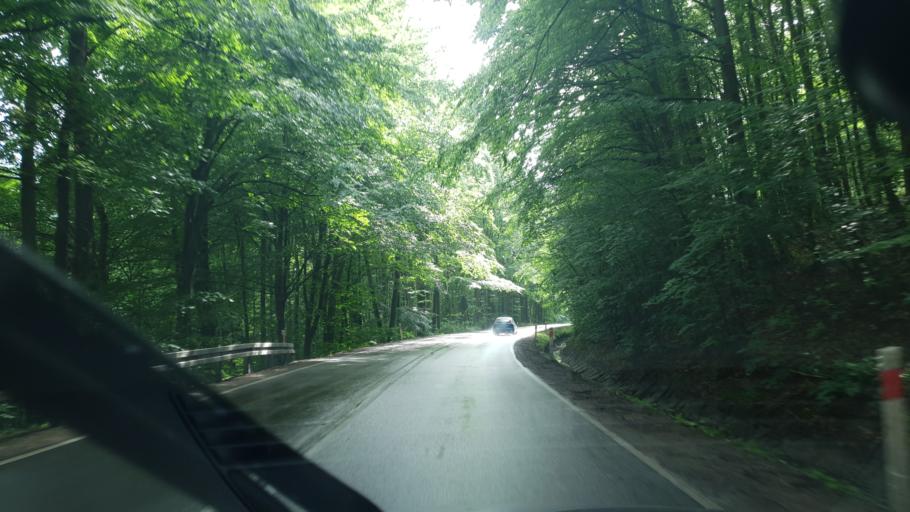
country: PL
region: Pomeranian Voivodeship
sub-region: Powiat kartuski
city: Kartuzy
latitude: 54.3188
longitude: 18.1775
